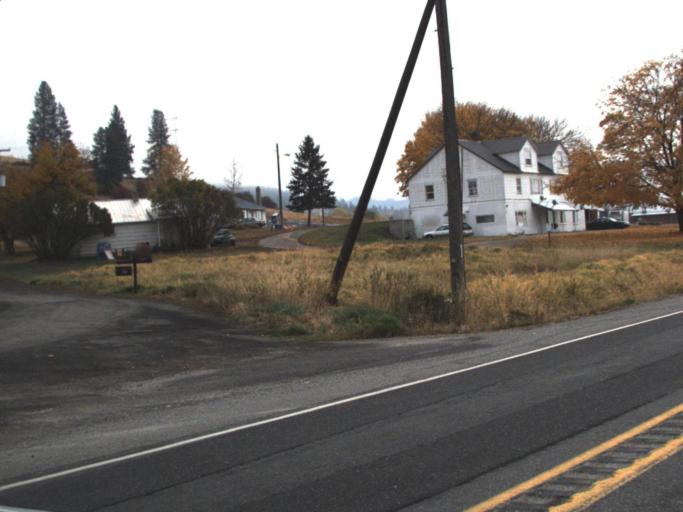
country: US
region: Washington
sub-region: Stevens County
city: Colville
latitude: 48.5651
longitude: -117.9352
